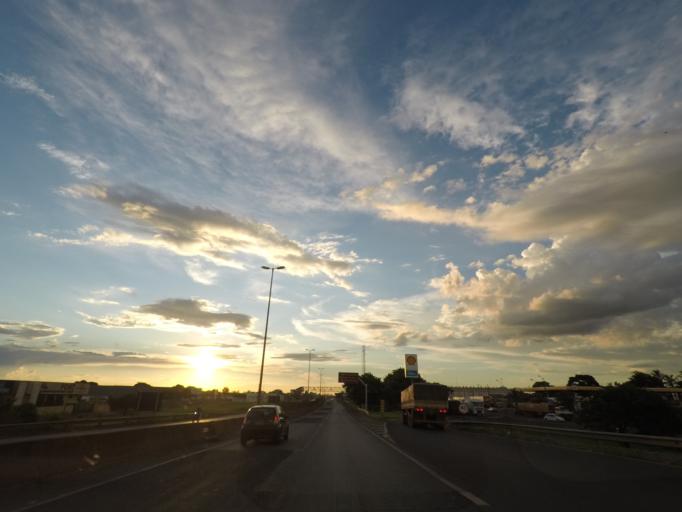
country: BR
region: Minas Gerais
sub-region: Uberaba
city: Uberaba
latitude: -19.7779
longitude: -47.9258
